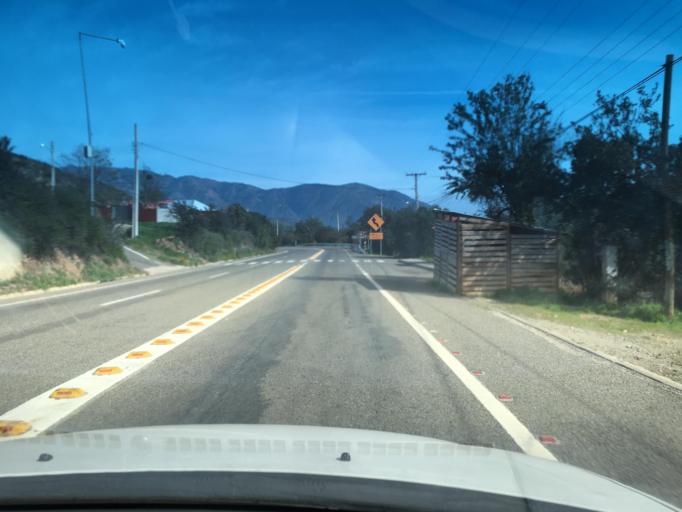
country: CL
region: Valparaiso
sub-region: Provincia de San Felipe
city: Llaillay
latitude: -33.0595
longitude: -71.0330
